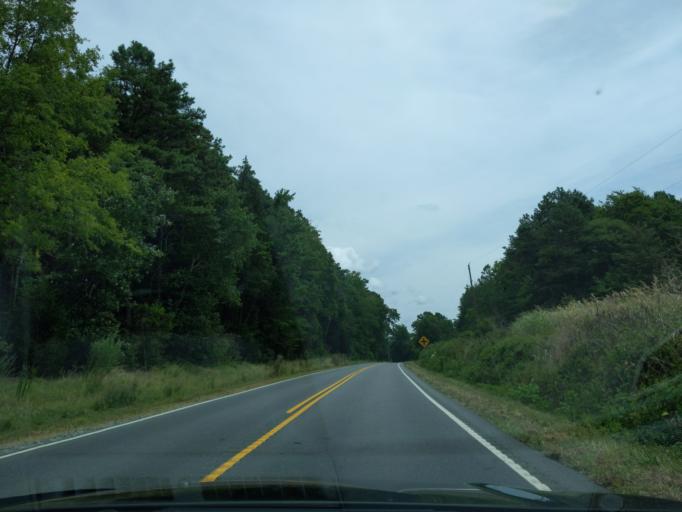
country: US
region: North Carolina
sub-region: Cabarrus County
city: Mount Pleasant
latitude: 35.4547
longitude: -80.3436
